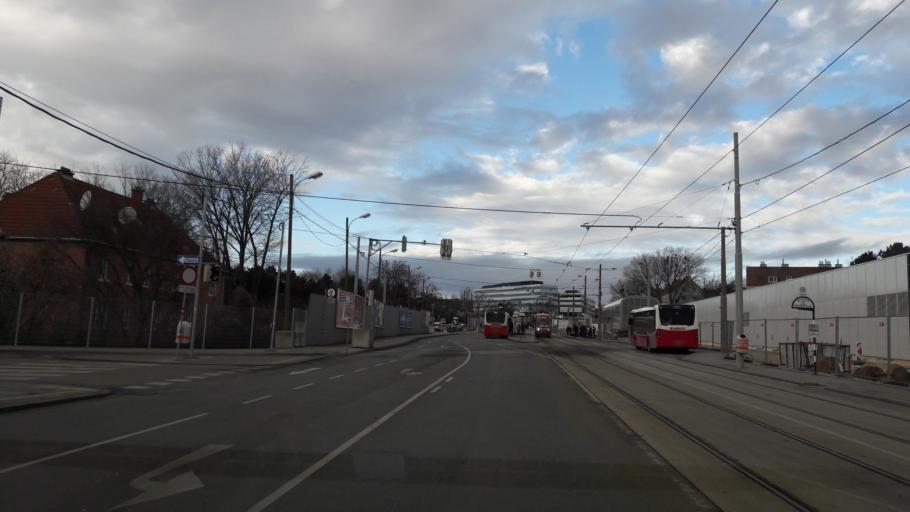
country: AT
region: Lower Austria
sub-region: Politischer Bezirk Wien-Umgebung
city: Leopoldsdorf
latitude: 48.1528
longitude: 16.3821
